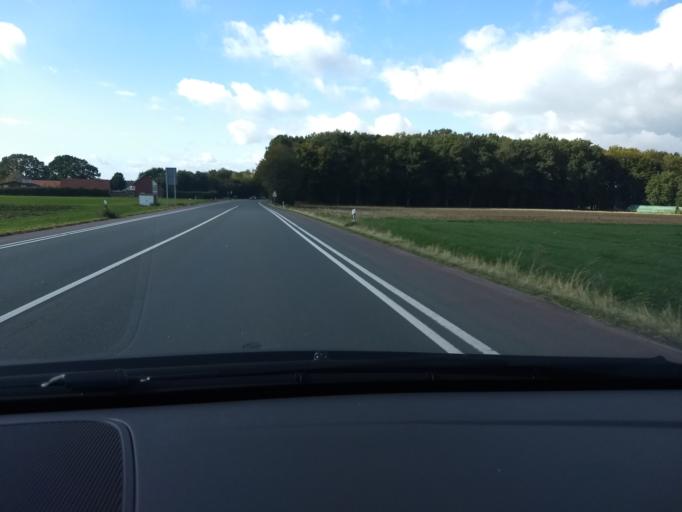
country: DE
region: North Rhine-Westphalia
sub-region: Regierungsbezirk Munster
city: Heiden
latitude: 51.8247
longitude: 6.9118
